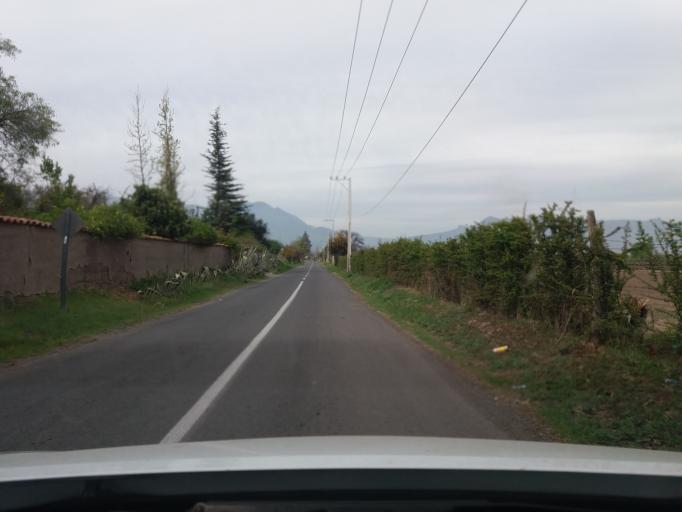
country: CL
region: Valparaiso
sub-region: Provincia de Los Andes
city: Los Andes
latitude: -32.8290
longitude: -70.6599
